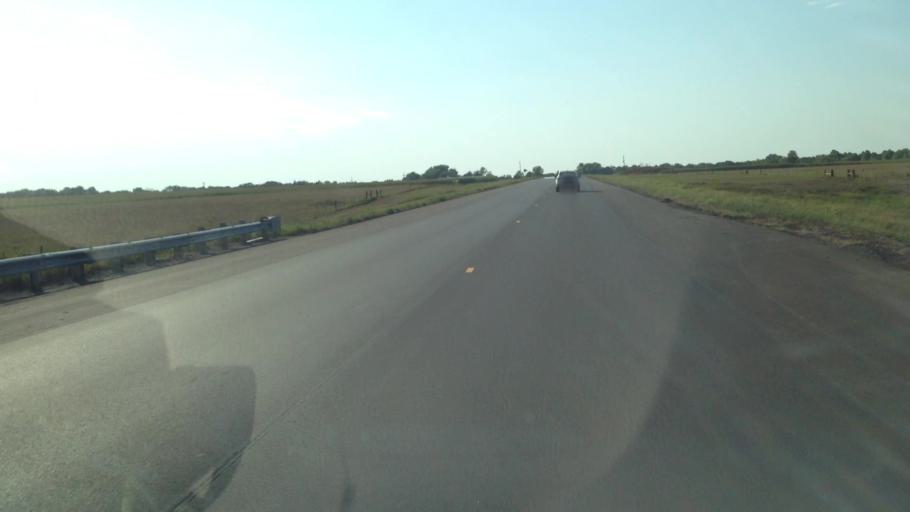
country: US
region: Kansas
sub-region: Franklin County
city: Ottawa
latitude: 38.4677
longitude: -95.2599
